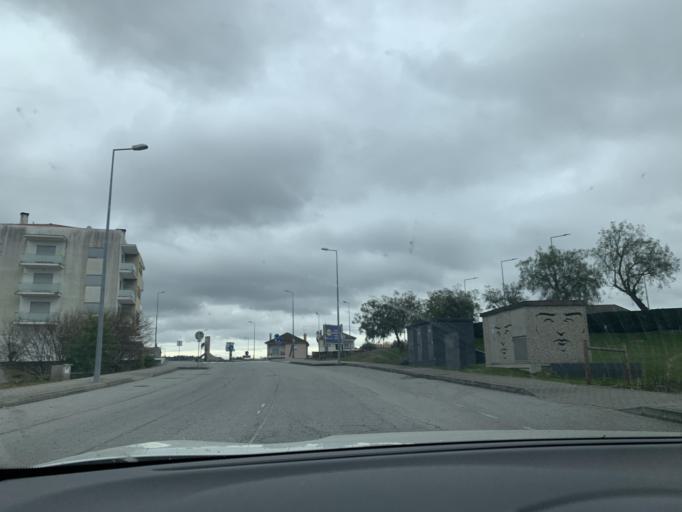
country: PT
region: Viseu
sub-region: Mangualde
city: Mangualde
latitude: 40.6099
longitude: -7.7627
